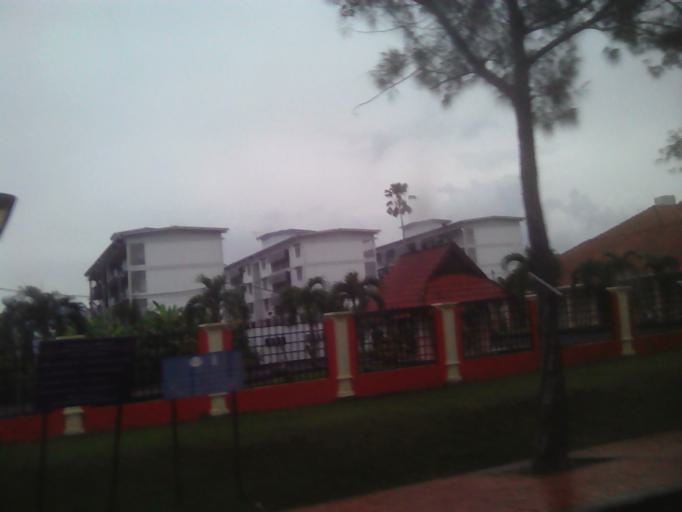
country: MY
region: Kedah
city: Kulim
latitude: 5.3700
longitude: 100.5578
